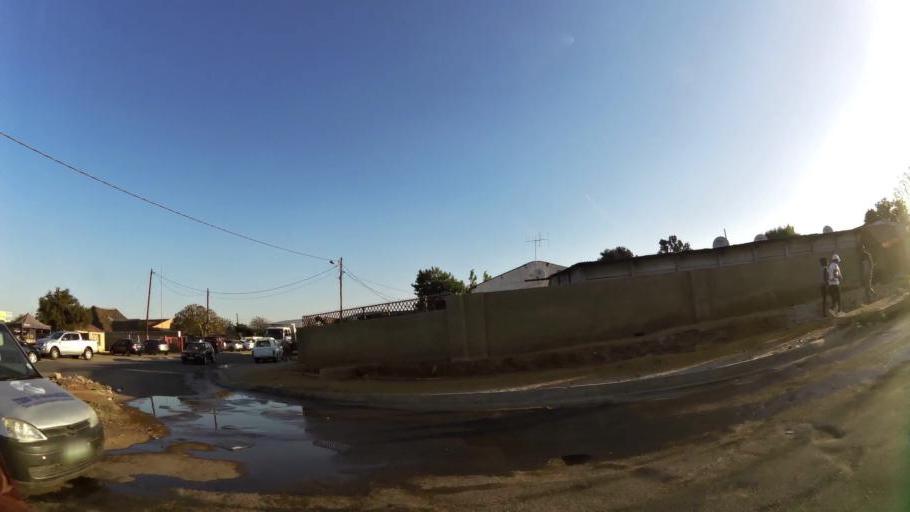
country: ZA
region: North-West
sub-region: Bojanala Platinum District Municipality
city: Rustenburg
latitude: -25.6366
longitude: 27.2118
